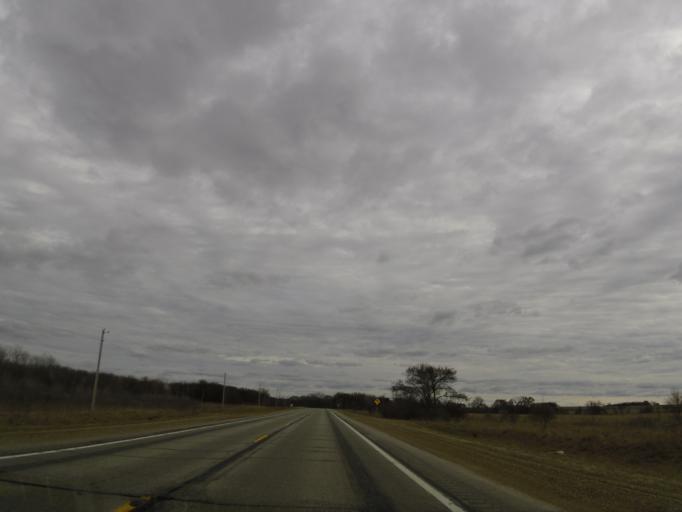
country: US
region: Iowa
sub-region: Howard County
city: Cresco
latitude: 43.4641
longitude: -92.3116
